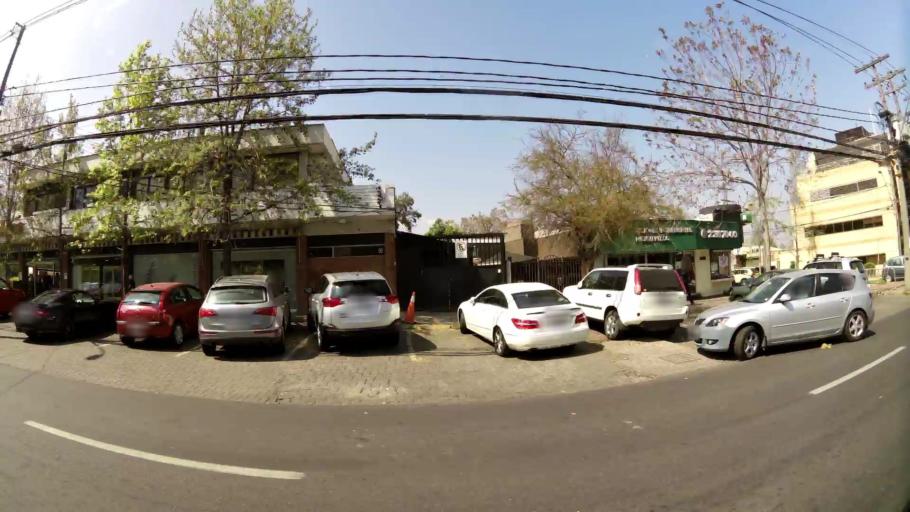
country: CL
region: Santiago Metropolitan
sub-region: Provincia de Santiago
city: Villa Presidente Frei, Nunoa, Santiago, Chile
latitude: -33.3876
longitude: -70.5768
